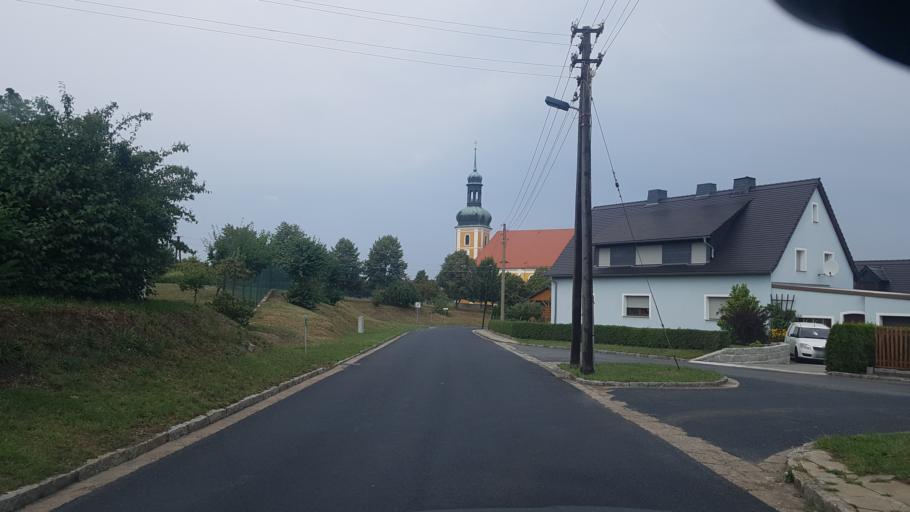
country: DE
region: Saxony
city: Horka
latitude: 51.2849
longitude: 14.2282
